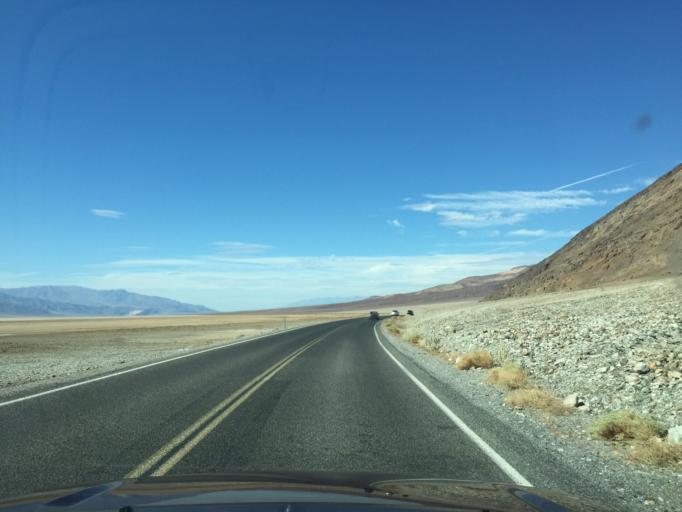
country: US
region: Nevada
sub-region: Nye County
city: Beatty
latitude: 36.2401
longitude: -116.7713
